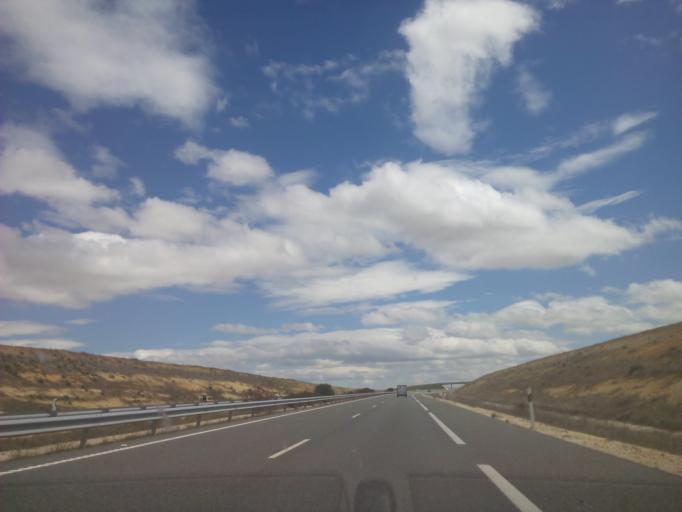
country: ES
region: Castille and Leon
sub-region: Provincia de Salamanca
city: Calvarrasa de Abajo
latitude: 40.9295
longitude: -5.5469
